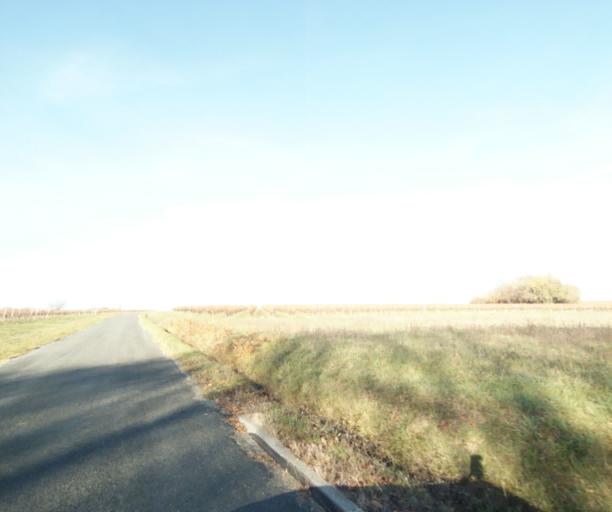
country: FR
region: Poitou-Charentes
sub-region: Departement de la Charente-Maritime
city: Cherac
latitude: 45.7326
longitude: -0.4521
